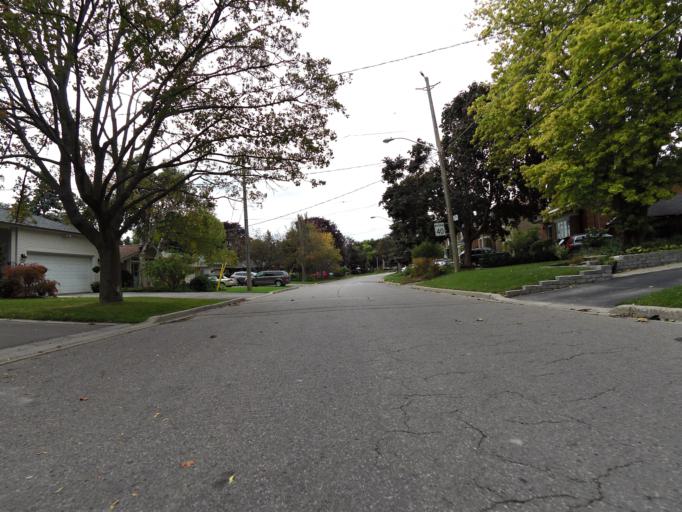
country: CA
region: Ontario
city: Scarborough
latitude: 43.7008
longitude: -79.2472
